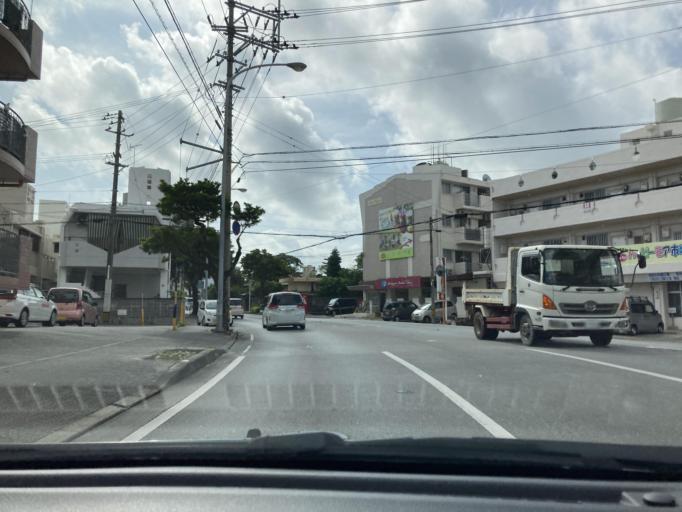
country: JP
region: Okinawa
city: Ginowan
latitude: 26.2601
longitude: 127.7640
